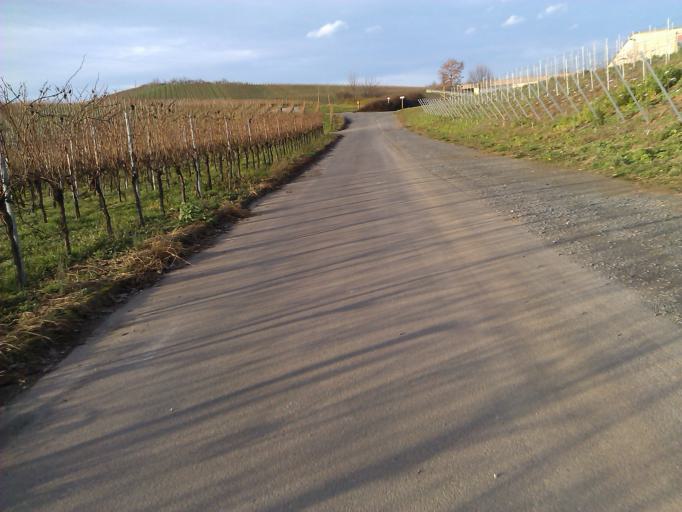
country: DE
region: Baden-Wuerttemberg
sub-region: Regierungsbezirk Stuttgart
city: Erlenbach
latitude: 49.1665
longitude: 9.2413
